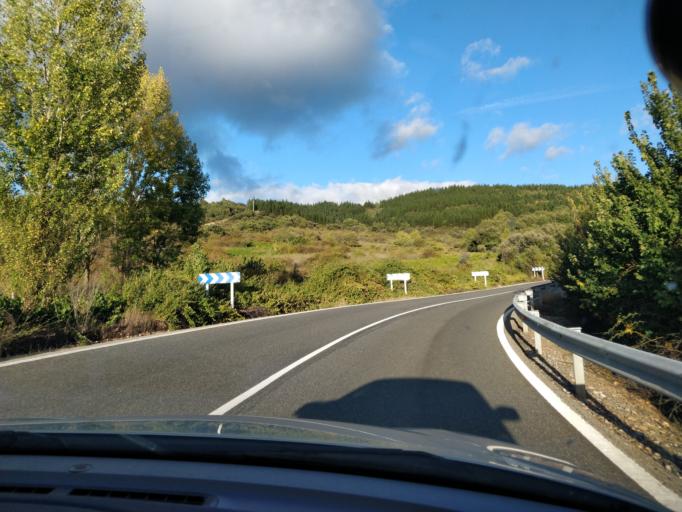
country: ES
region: Castille and Leon
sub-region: Provincia de Leon
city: Borrenes
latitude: 42.4981
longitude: -6.7203
